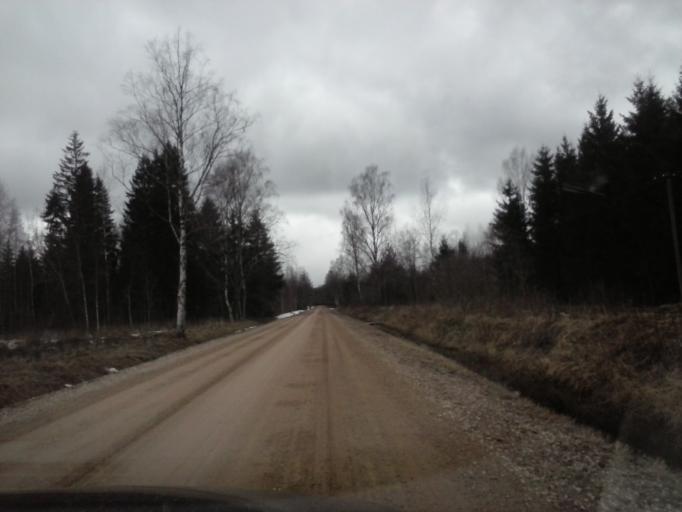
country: EE
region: Jogevamaa
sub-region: Mustvee linn
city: Mustvee
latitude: 59.0824
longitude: 26.8398
